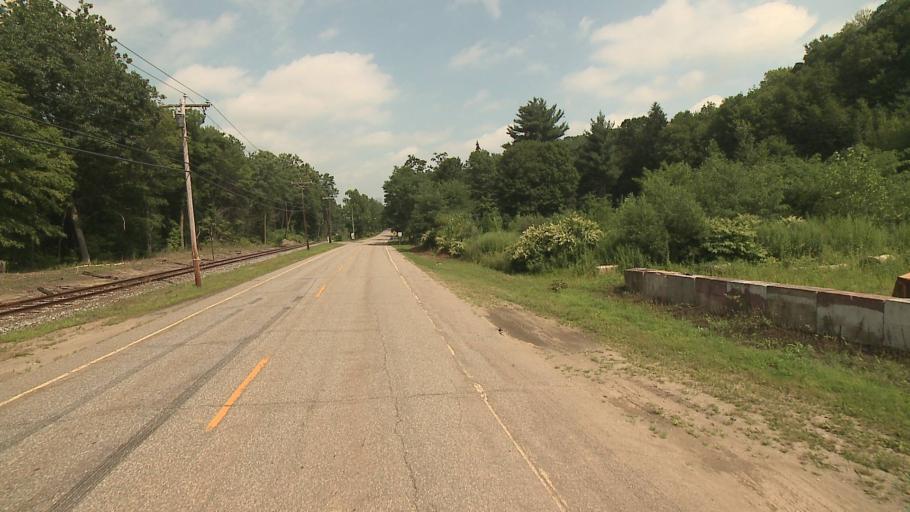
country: US
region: Connecticut
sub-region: Litchfield County
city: Thomaston
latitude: 41.6457
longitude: -73.0776
